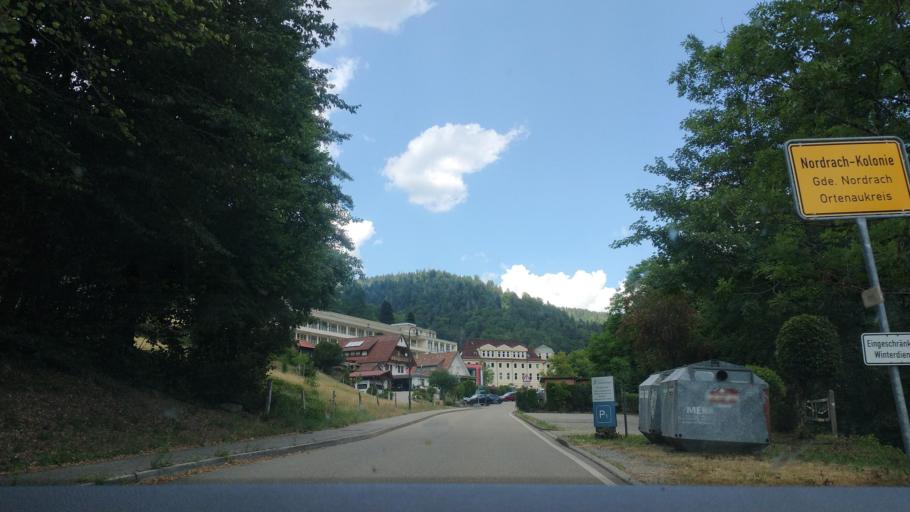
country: DE
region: Baden-Wuerttemberg
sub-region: Freiburg Region
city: Nordrach
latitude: 48.4291
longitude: 8.1236
